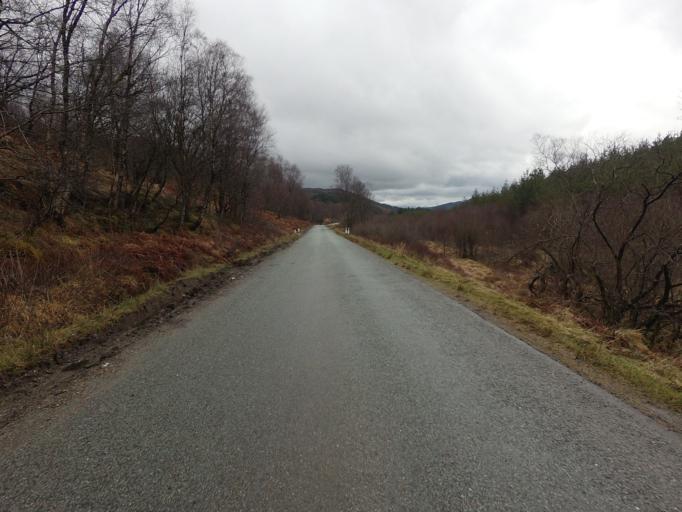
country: GB
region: Scotland
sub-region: West Dunbartonshire
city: Balloch
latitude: 56.2409
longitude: -4.5694
